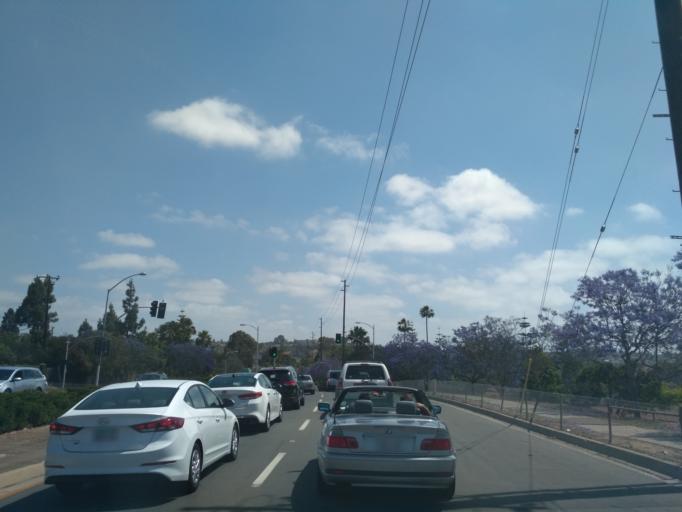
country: US
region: California
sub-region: San Diego County
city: La Jolla
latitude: 32.8024
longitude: -117.2273
